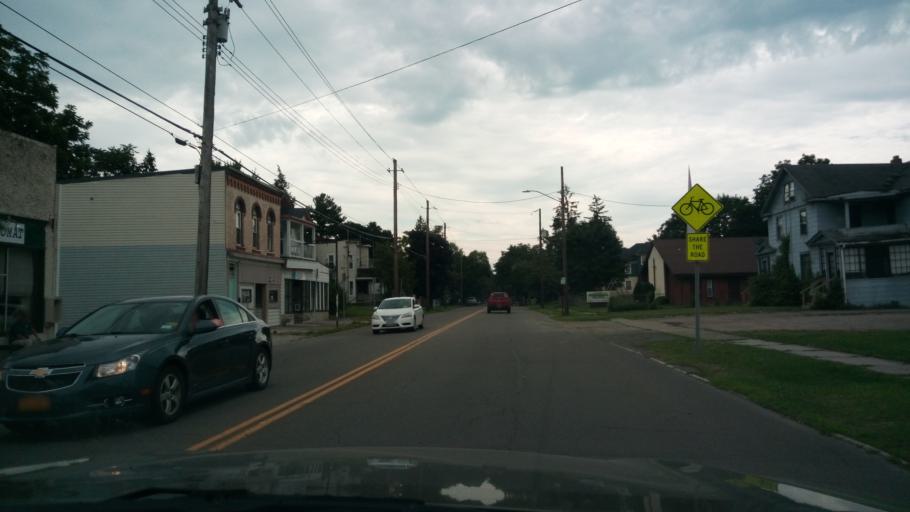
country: US
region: New York
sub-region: Chemung County
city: Elmira
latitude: 42.1078
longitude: -76.8057
